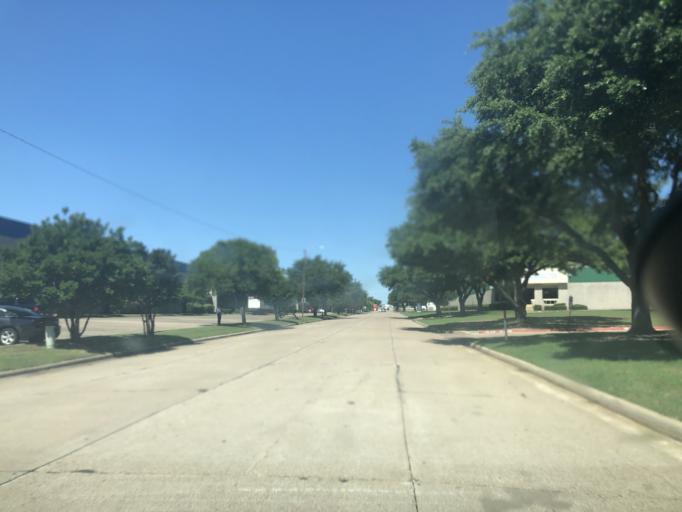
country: US
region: Texas
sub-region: Dallas County
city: Grand Prairie
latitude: 32.7829
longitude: -97.0436
